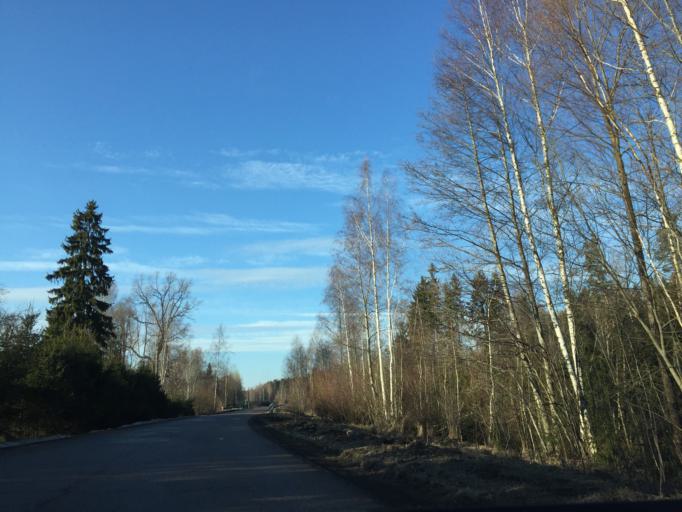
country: LV
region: Lecava
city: Iecava
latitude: 56.6920
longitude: 24.0896
